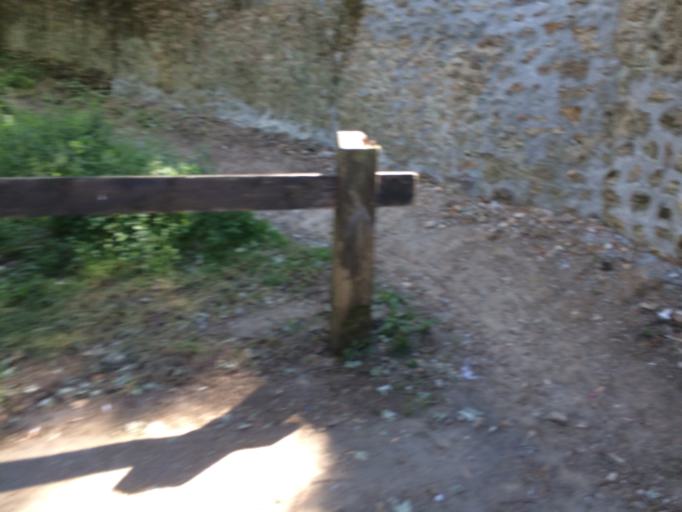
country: FR
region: Ile-de-France
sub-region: Departement de l'Essonne
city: Vauhallan
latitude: 48.7307
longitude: 2.2043
